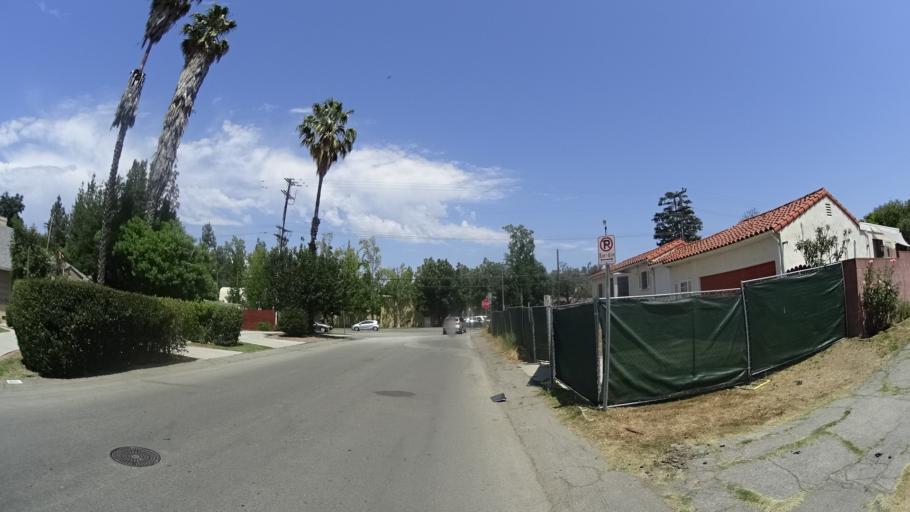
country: US
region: California
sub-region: Los Angeles County
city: Sherman Oaks
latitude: 34.1440
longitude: -118.4143
